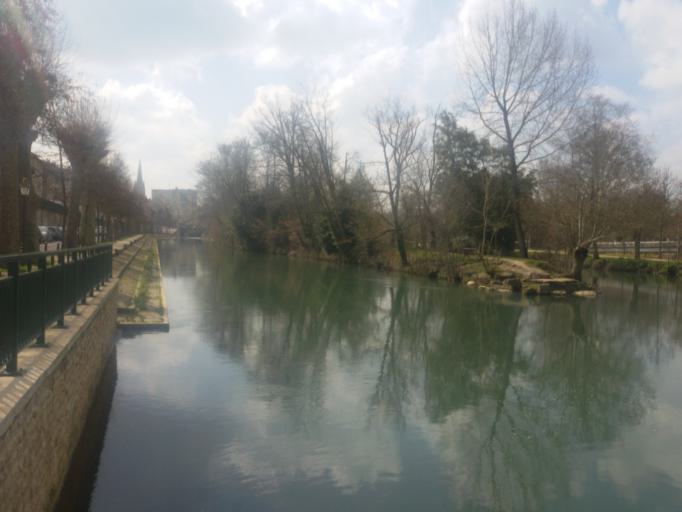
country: FR
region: Poitou-Charentes
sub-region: Departement des Deux-Sevres
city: Niort
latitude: 46.3297
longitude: -0.4625
